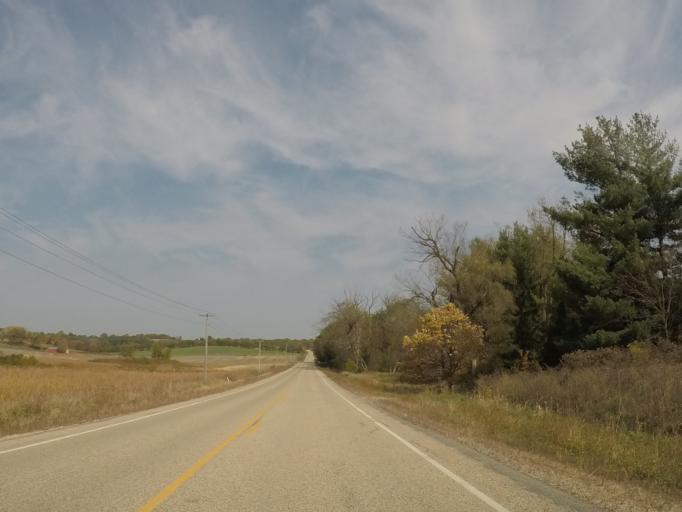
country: US
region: Wisconsin
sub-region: Dane County
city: Cross Plains
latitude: 43.0346
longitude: -89.6163
